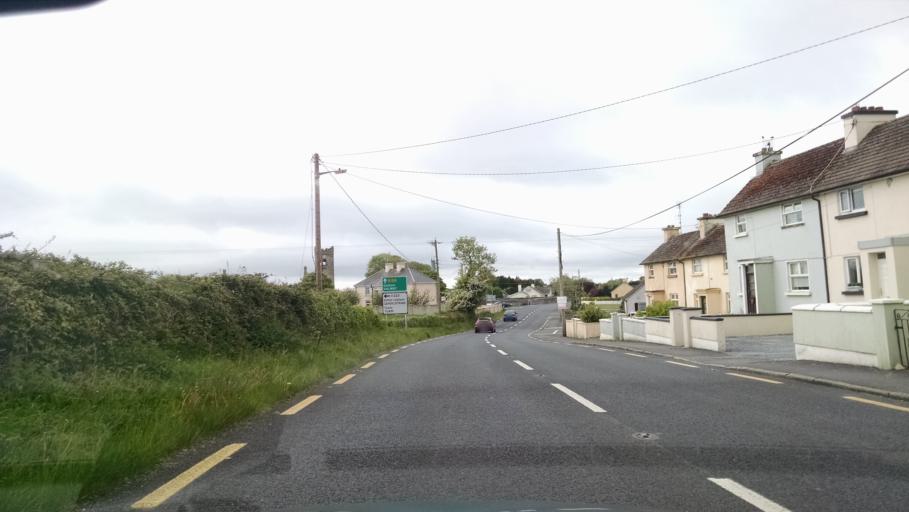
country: IE
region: Connaught
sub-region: County Galway
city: Moycullen
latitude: 53.4755
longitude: -9.0935
